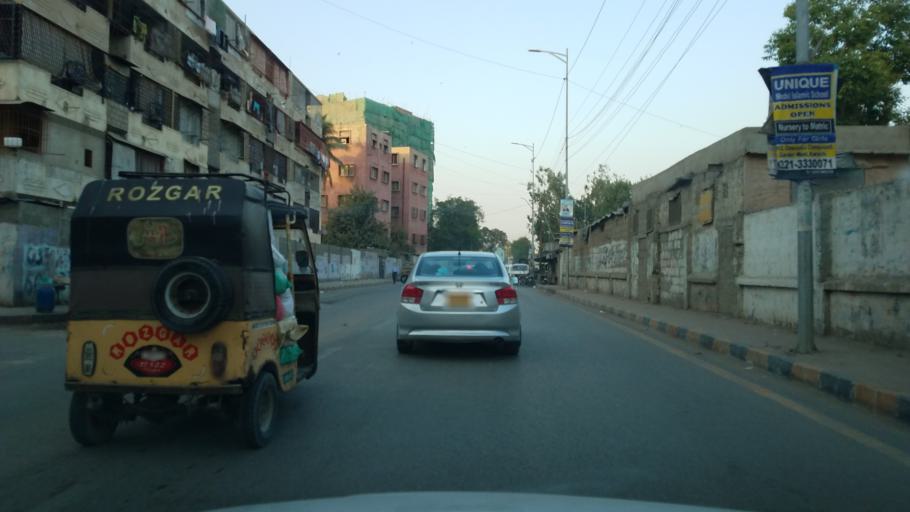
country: PK
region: Sindh
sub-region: Karachi District
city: Karachi
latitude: 24.8802
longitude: 67.0214
